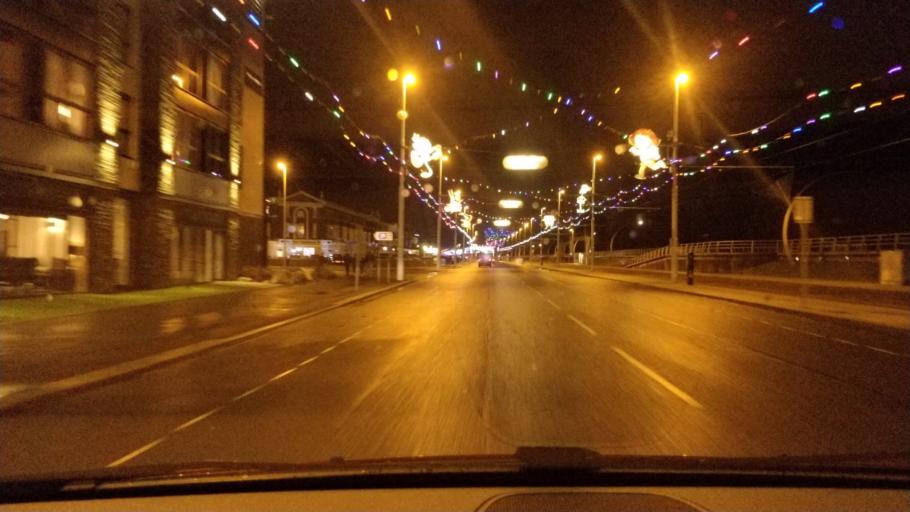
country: GB
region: England
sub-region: Blackpool
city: Blackpool
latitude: 53.7890
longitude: -3.0579
